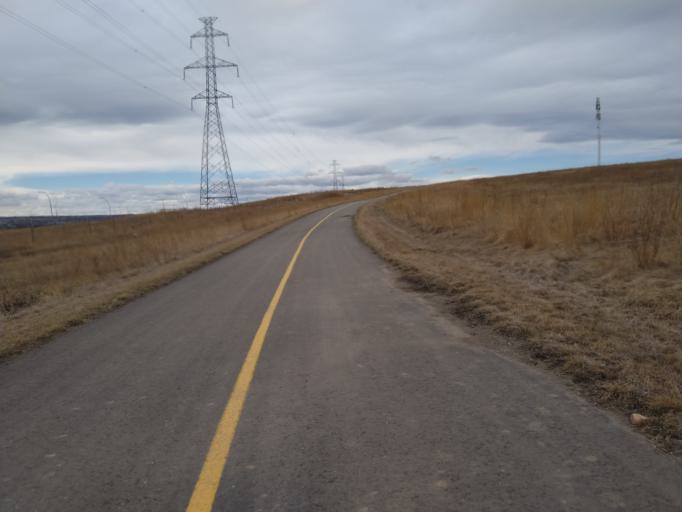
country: CA
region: Alberta
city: Calgary
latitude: 51.1744
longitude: -114.0614
